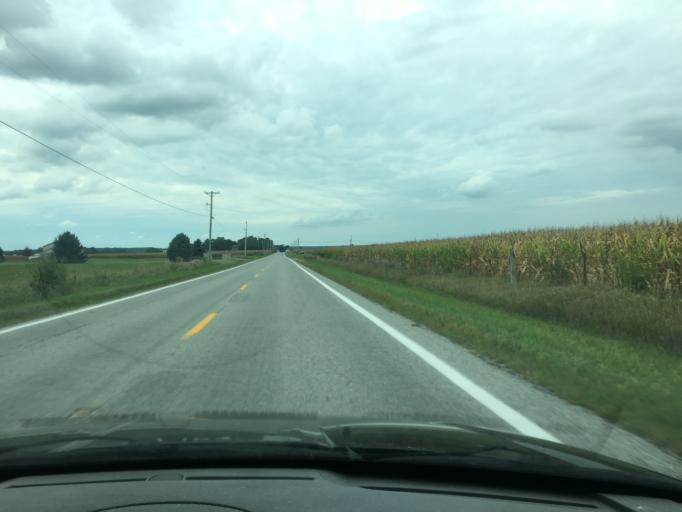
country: US
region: Ohio
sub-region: Champaign County
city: Urbana
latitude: 40.1538
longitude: -83.7228
